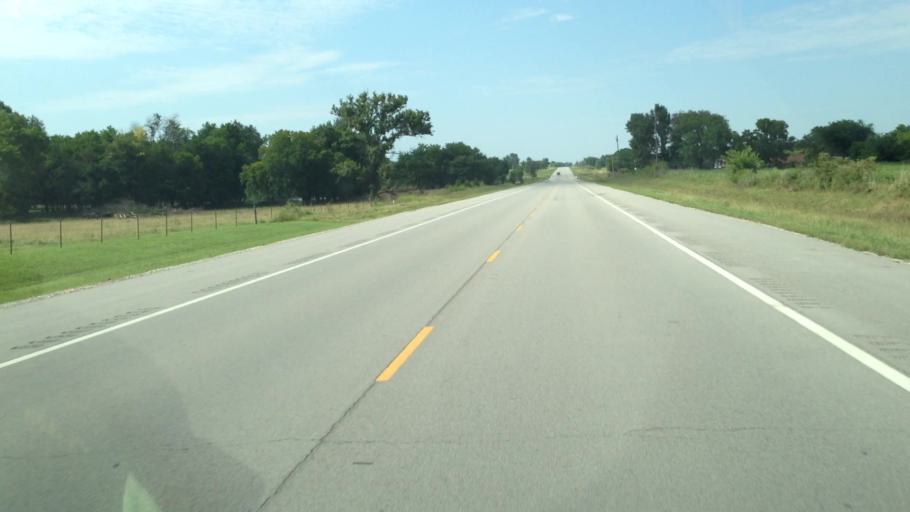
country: US
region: Kansas
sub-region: Labette County
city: Parsons
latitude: 37.2683
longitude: -95.2672
